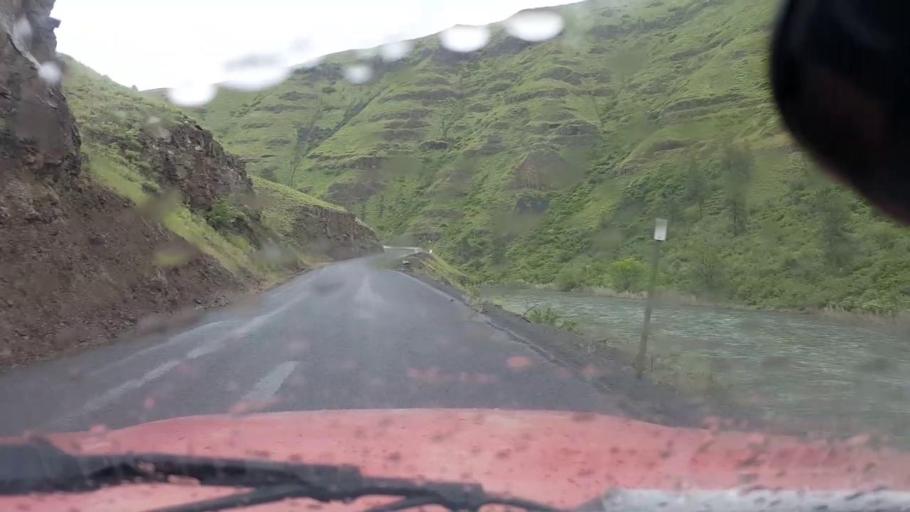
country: US
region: Washington
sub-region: Asotin County
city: Asotin
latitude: 46.0314
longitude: -117.2972
